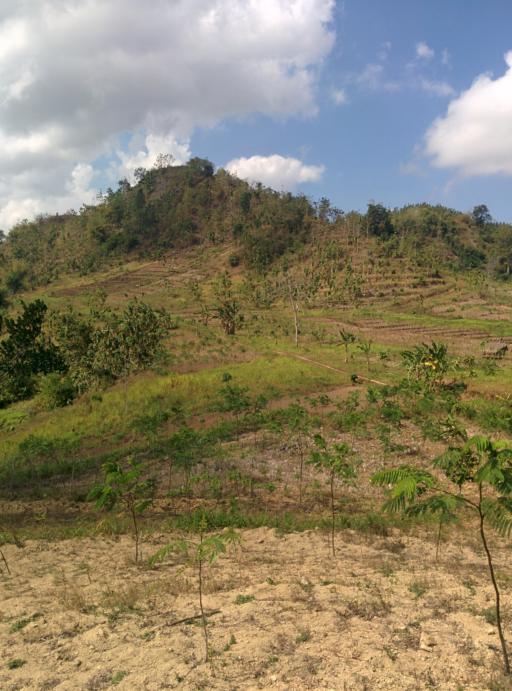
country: ID
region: East Java
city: Bacem
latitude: -8.2046
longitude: 112.2449
